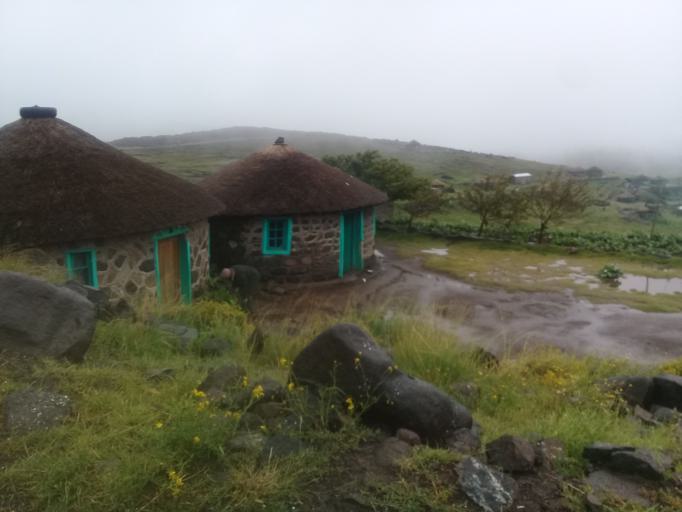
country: LS
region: Mokhotlong
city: Mokhotlong
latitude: -29.3765
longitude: 28.9887
